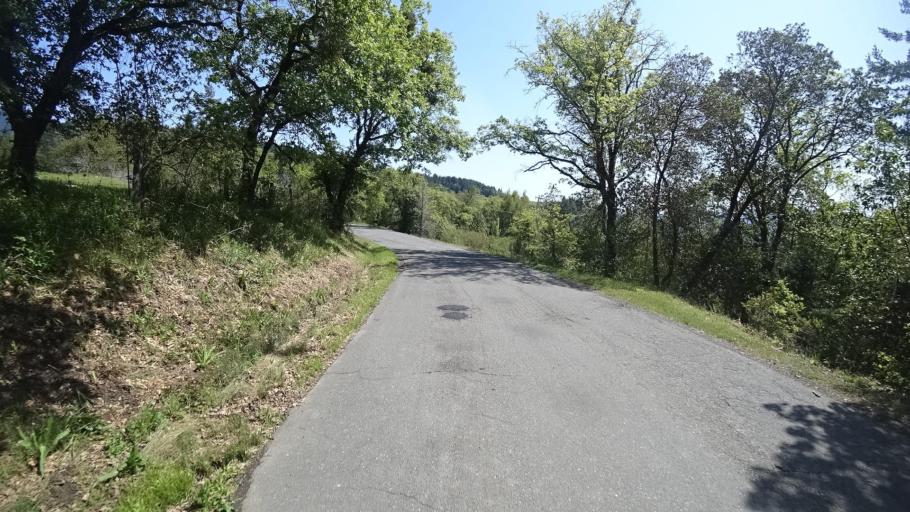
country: US
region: California
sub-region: Humboldt County
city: Redway
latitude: 40.2728
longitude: -123.6287
